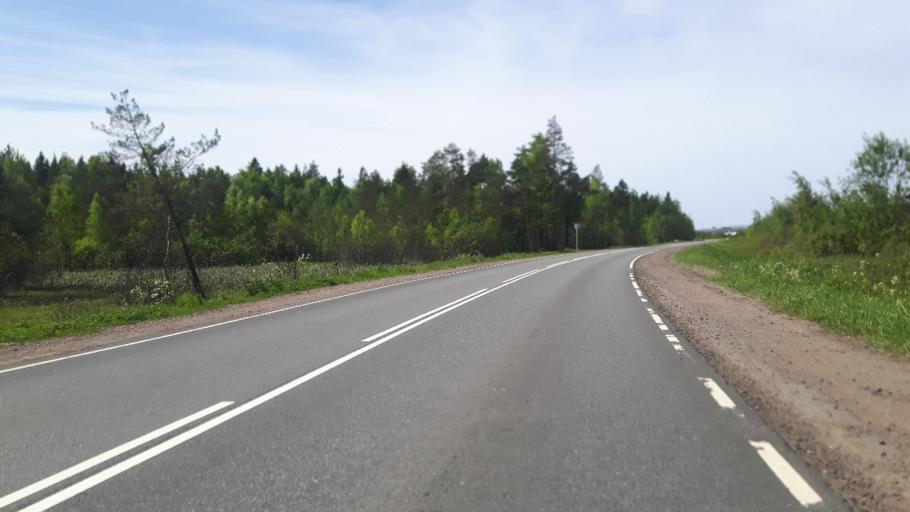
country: RU
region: Leningrad
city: Ust'-Luga
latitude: 59.6589
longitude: 28.4063
